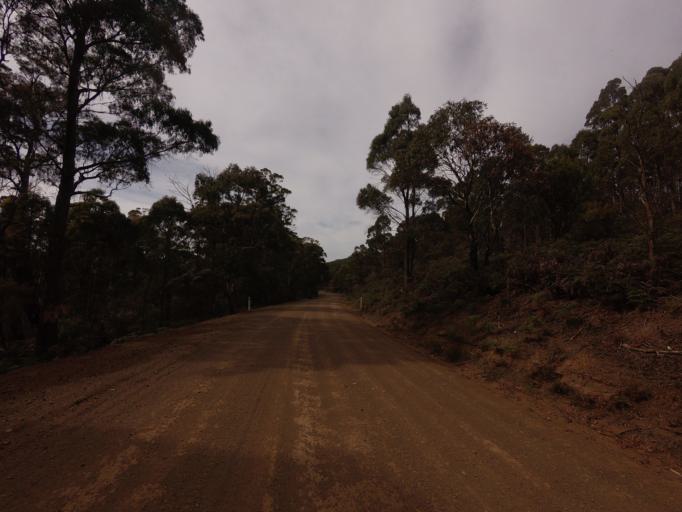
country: AU
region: Tasmania
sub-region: Sorell
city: Sorell
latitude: -42.4891
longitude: 147.6204
